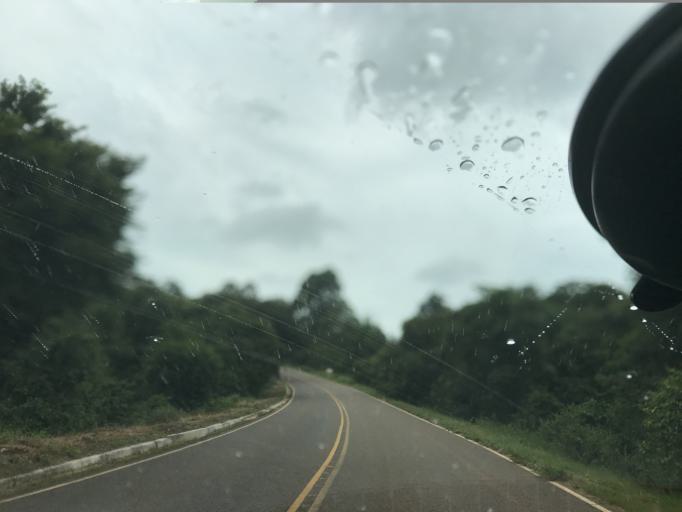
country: BR
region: Minas Gerais
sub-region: Conceicao Do Rio Verde
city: Conceicao do Rio Verde
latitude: -21.6859
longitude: -45.0159
